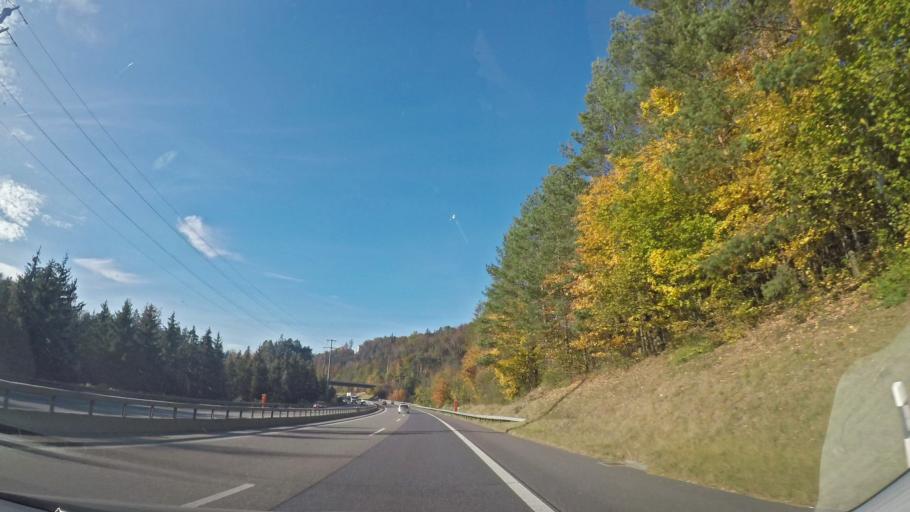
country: CH
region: Bern
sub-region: Frutigen-Niedersimmental District
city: Wimmis
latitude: 46.7083
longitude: 7.6337
